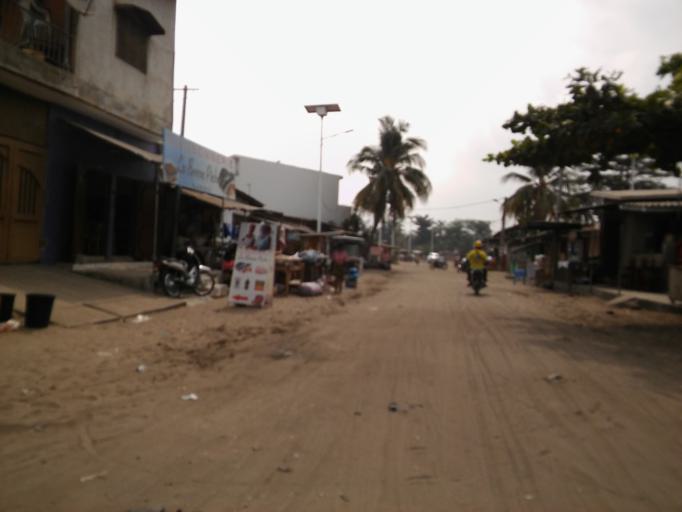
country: BJ
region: Littoral
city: Cotonou
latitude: 6.3914
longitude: 2.3836
